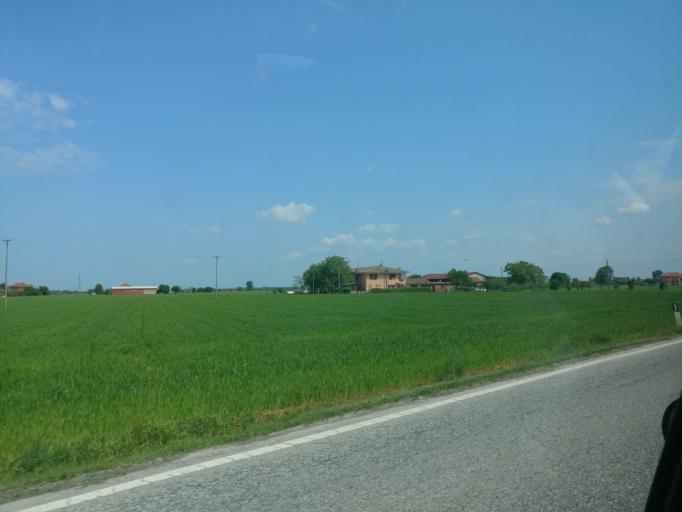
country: IT
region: Piedmont
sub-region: Provincia di Torino
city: Cavour
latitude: 44.7539
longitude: 7.4041
